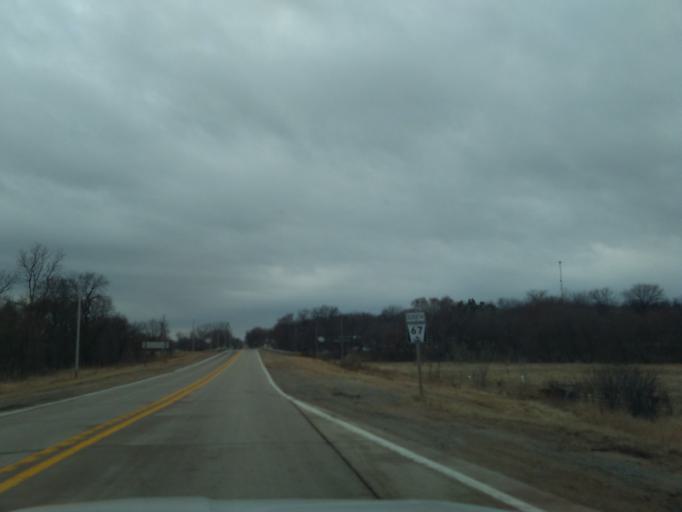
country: US
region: Nebraska
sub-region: Otoe County
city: Syracuse
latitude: 40.6755
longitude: -96.0301
